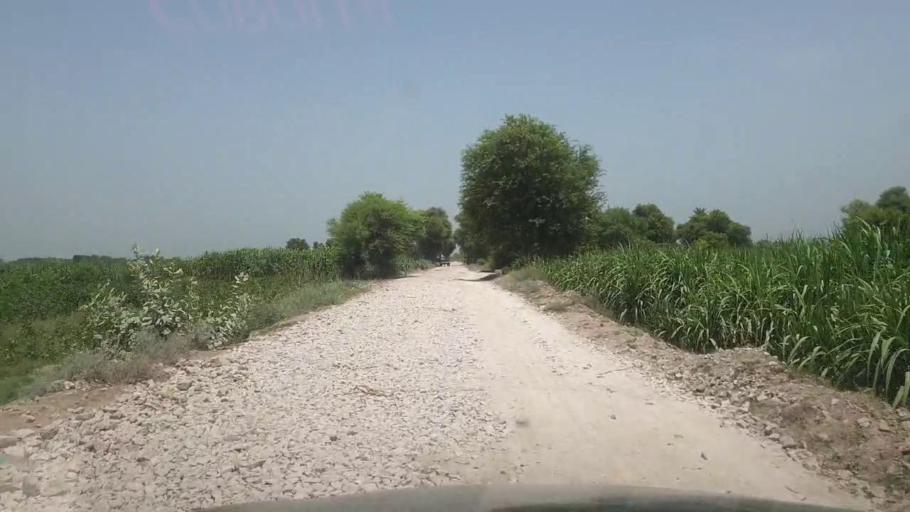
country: PK
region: Sindh
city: Sobhadero
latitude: 27.3280
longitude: 68.3545
